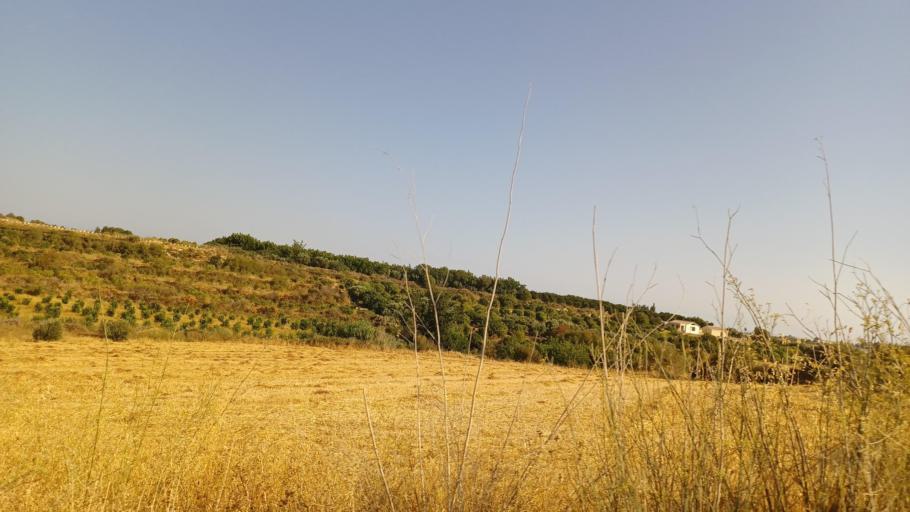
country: CY
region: Pafos
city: Polis
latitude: 35.0180
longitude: 32.4214
